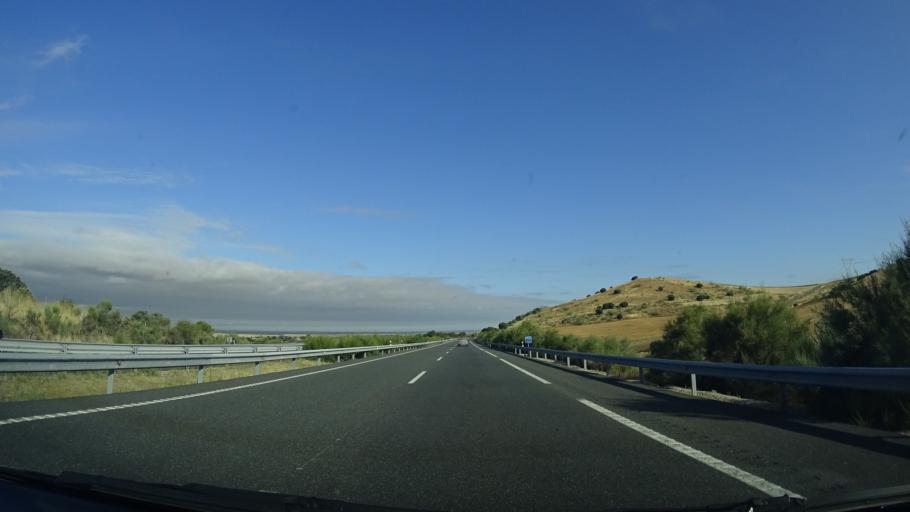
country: ES
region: Castille and Leon
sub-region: Provincia de Segovia
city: Labajos
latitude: 40.8374
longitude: -4.5324
